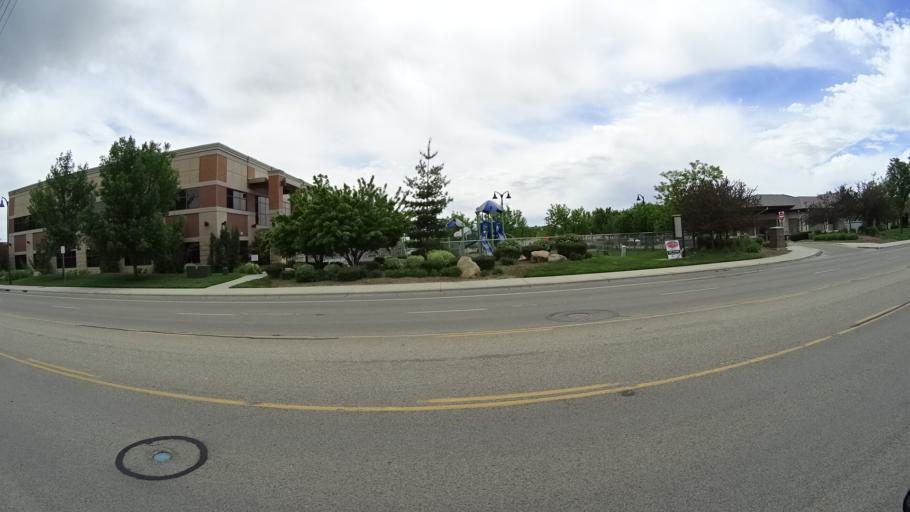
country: US
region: Idaho
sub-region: Ada County
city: Meridian
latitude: 43.5904
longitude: -116.3602
